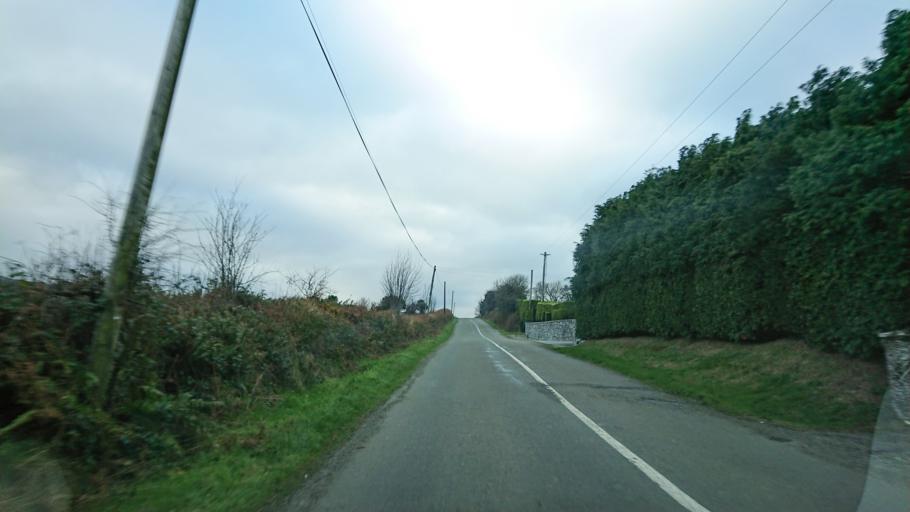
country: IE
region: Munster
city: Carrick-on-Suir
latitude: 52.3197
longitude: -7.5586
